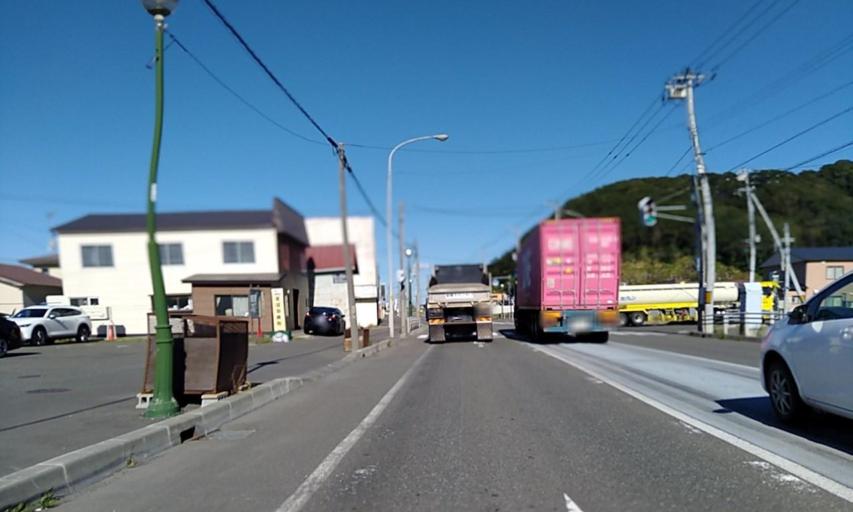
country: JP
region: Hokkaido
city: Shizunai-furukawacho
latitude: 42.4255
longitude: 142.2237
